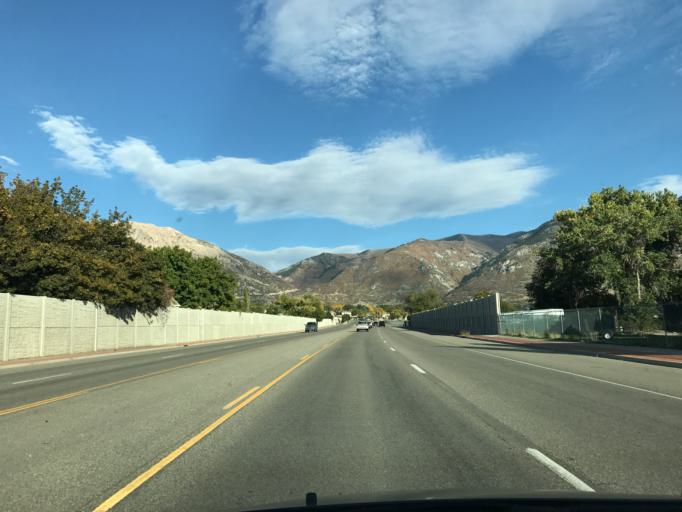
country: US
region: Utah
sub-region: Weber County
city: North Ogden
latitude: 41.3058
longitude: -111.9774
